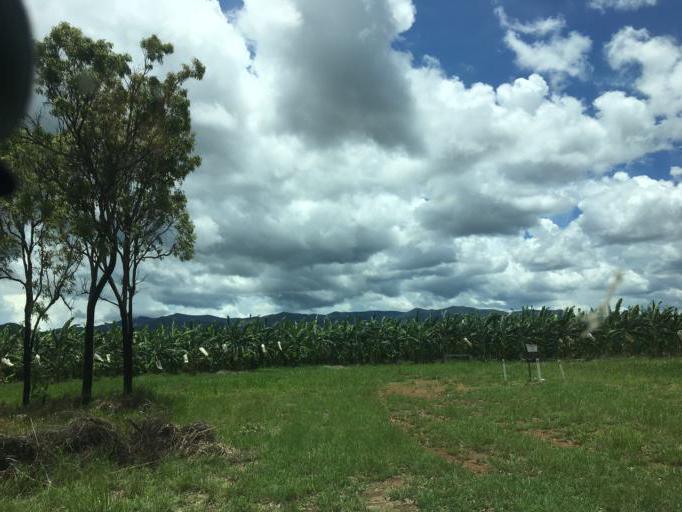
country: AU
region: Queensland
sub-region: Tablelands
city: Mareeba
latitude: -16.9883
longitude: 145.5260
